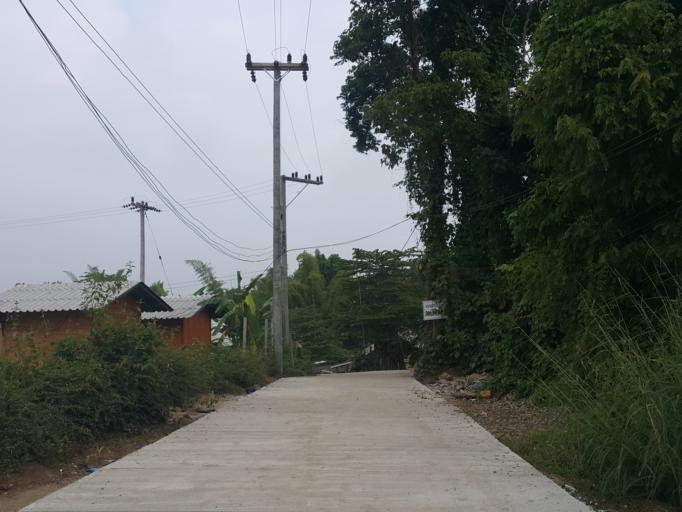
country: TH
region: Chiang Mai
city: Pai
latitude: 19.3618
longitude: 98.4493
